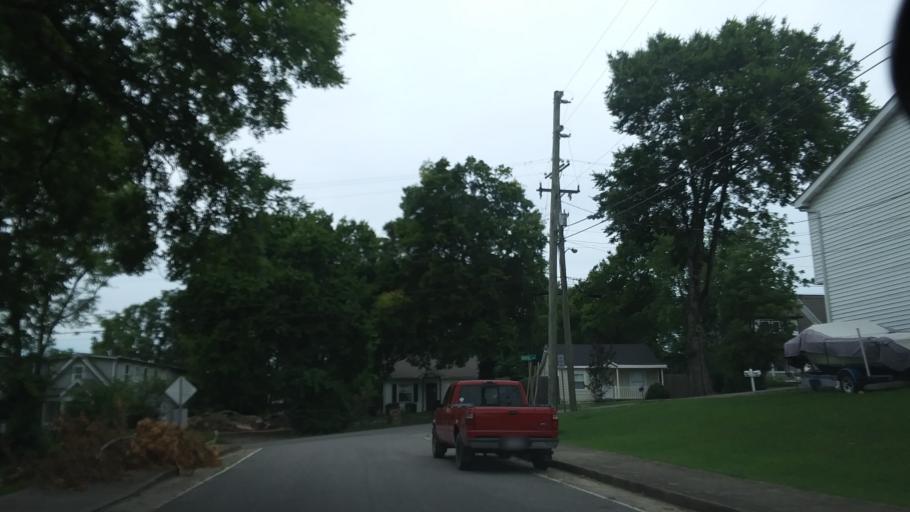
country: US
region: Tennessee
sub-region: Davidson County
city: Belle Meade
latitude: 36.1443
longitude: -86.8559
